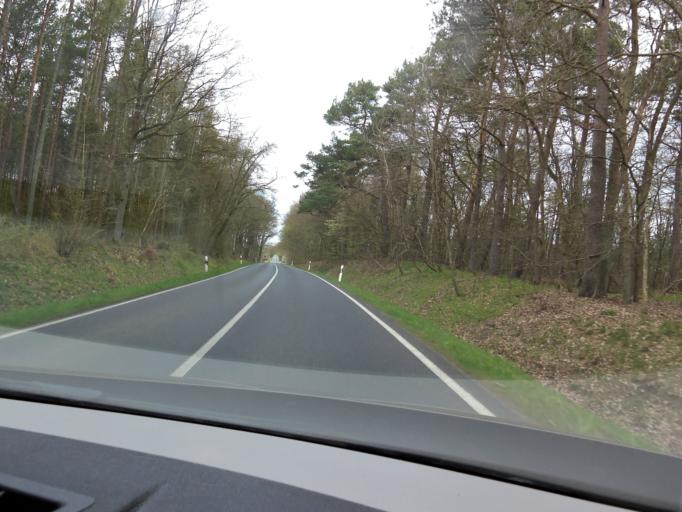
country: DE
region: Mecklenburg-Vorpommern
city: Gingst
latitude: 54.5058
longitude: 13.2768
